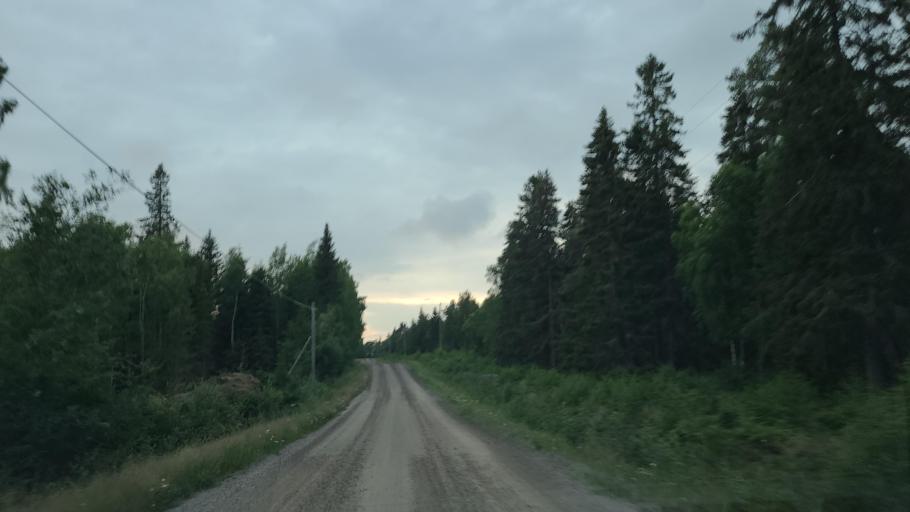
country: FI
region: Ostrobothnia
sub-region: Vaasa
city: Replot
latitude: 63.3197
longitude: 21.1466
